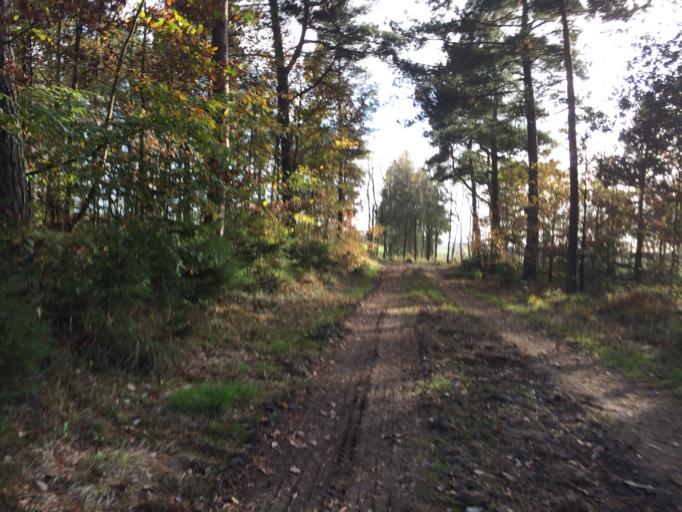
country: DK
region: Central Jutland
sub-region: Holstebro Kommune
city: Ulfborg
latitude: 56.2059
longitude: 8.4663
